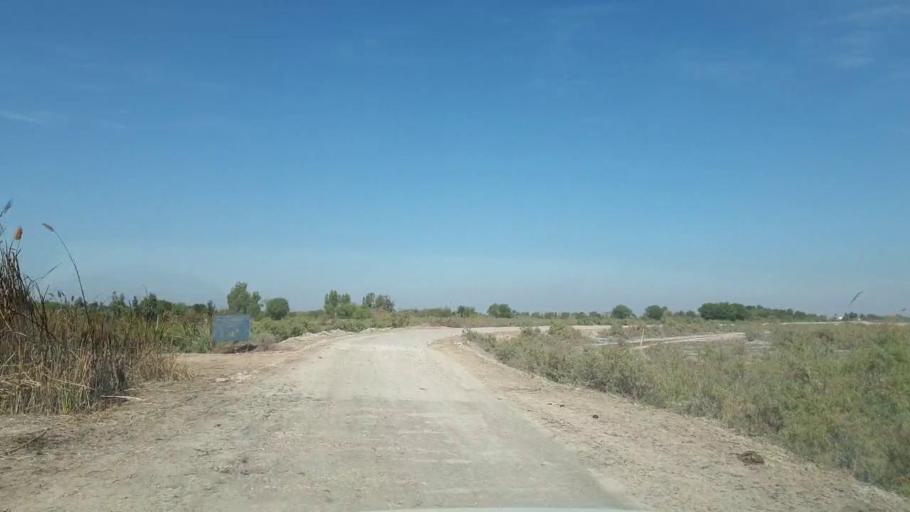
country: PK
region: Sindh
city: Pithoro
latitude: 25.6269
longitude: 69.2151
